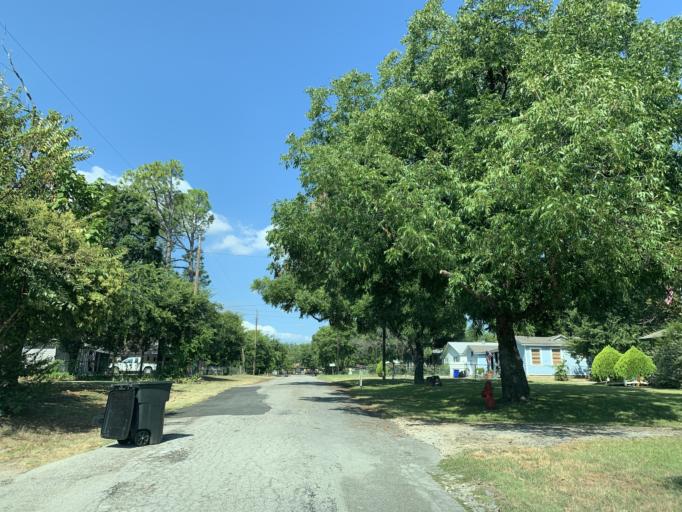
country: US
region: Texas
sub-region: Tarrant County
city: Azle
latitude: 32.8720
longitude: -97.5230
